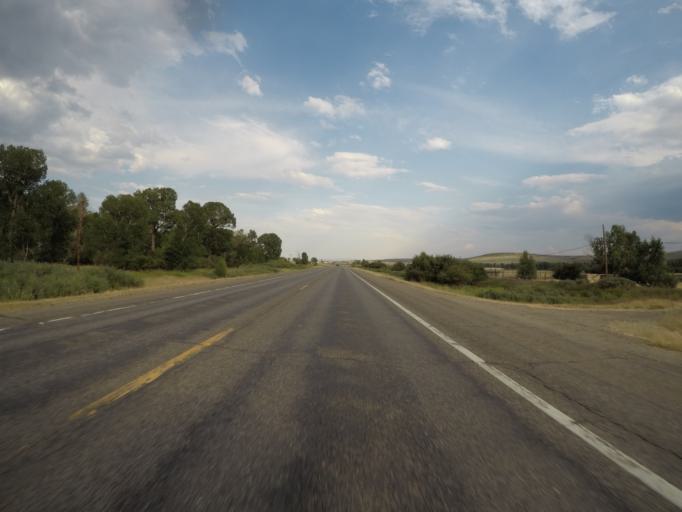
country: US
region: Colorado
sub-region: Moffat County
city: Craig
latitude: 40.5307
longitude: -107.4358
